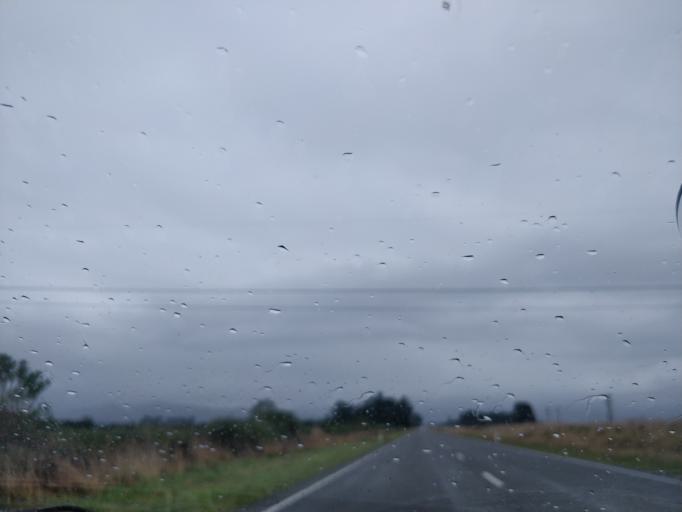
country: NZ
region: Canterbury
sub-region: Selwyn District
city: Darfield
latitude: -43.3838
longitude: 172.0104
